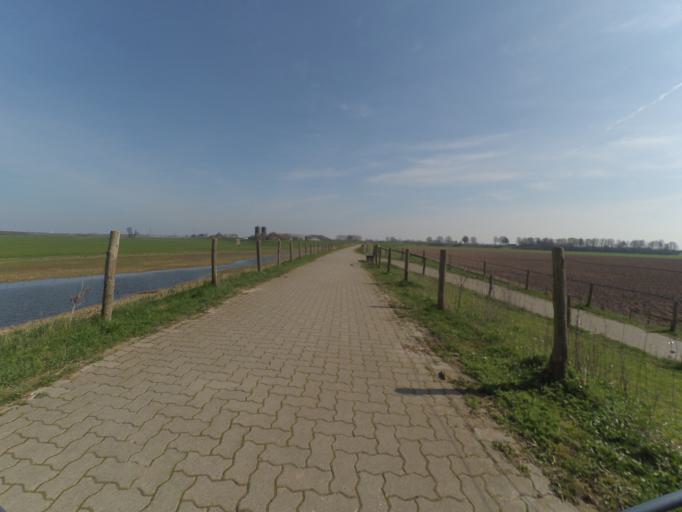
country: DE
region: North Rhine-Westphalia
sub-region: Regierungsbezirk Dusseldorf
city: Kleve
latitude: 51.8236
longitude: 6.1704
